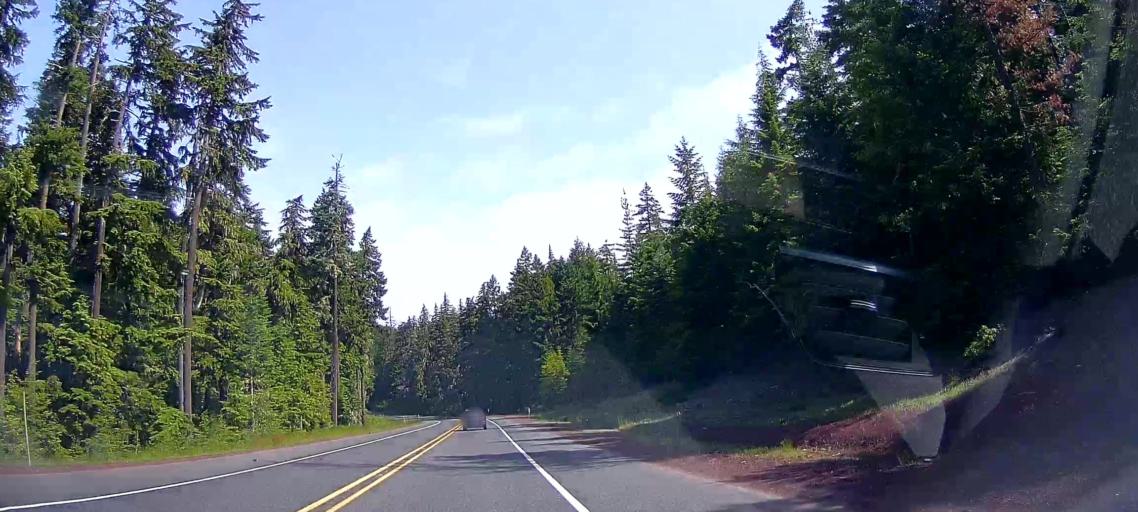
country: US
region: Oregon
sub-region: Clackamas County
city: Mount Hood Village
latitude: 45.2003
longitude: -121.6926
